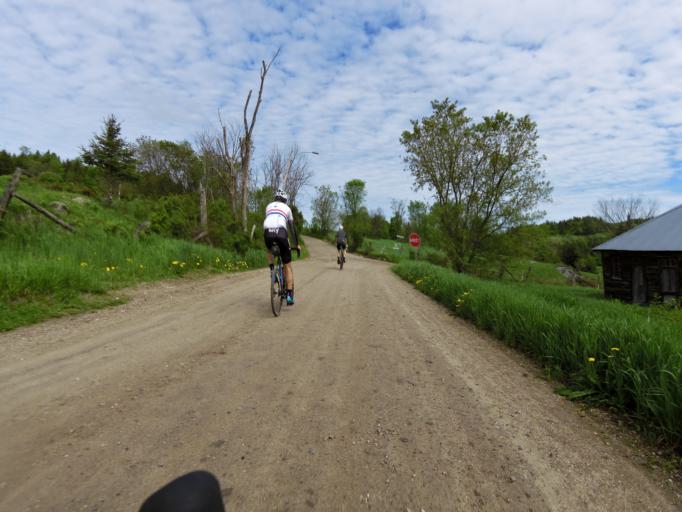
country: CA
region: Quebec
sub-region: Outaouais
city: Wakefield
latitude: 45.7725
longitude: -75.9253
